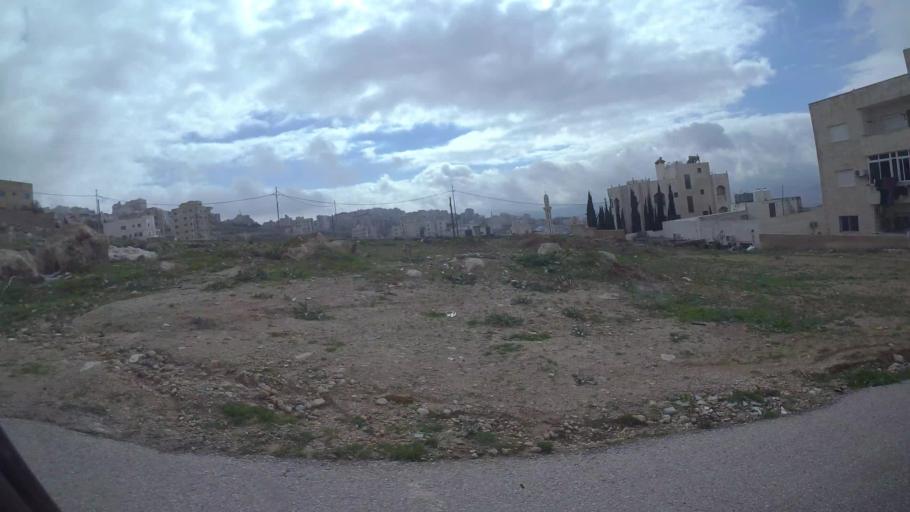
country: JO
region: Amman
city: Al Jubayhah
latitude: 32.0705
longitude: 35.8776
